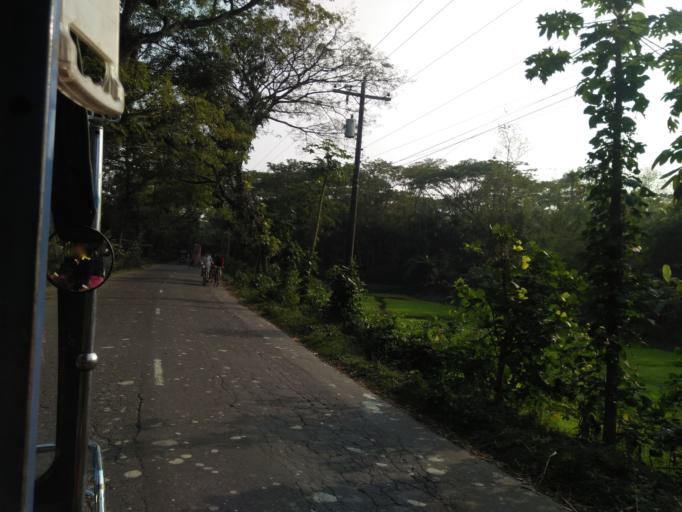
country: BD
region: Barisal
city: Bhola
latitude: 22.7121
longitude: 90.6398
